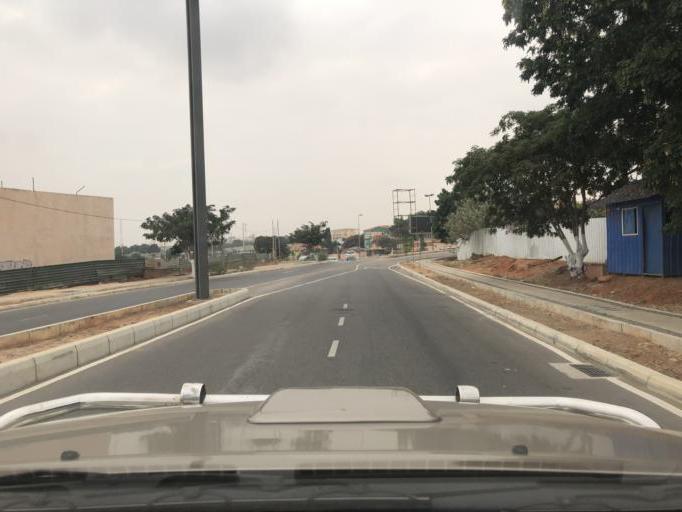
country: AO
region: Luanda
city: Luanda
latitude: -8.8930
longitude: 13.1768
